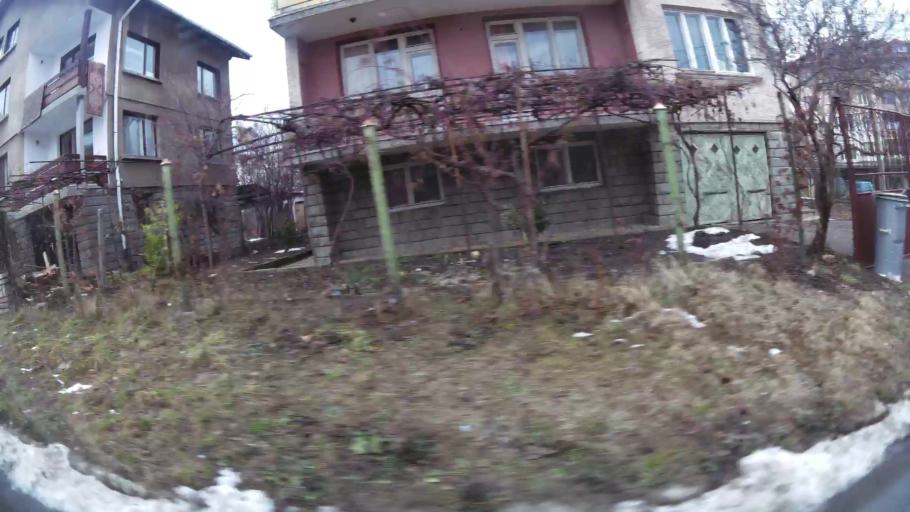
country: BG
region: Sofiya
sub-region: Obshtina Bozhurishte
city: Bozhurishte
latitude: 42.6796
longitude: 23.2385
